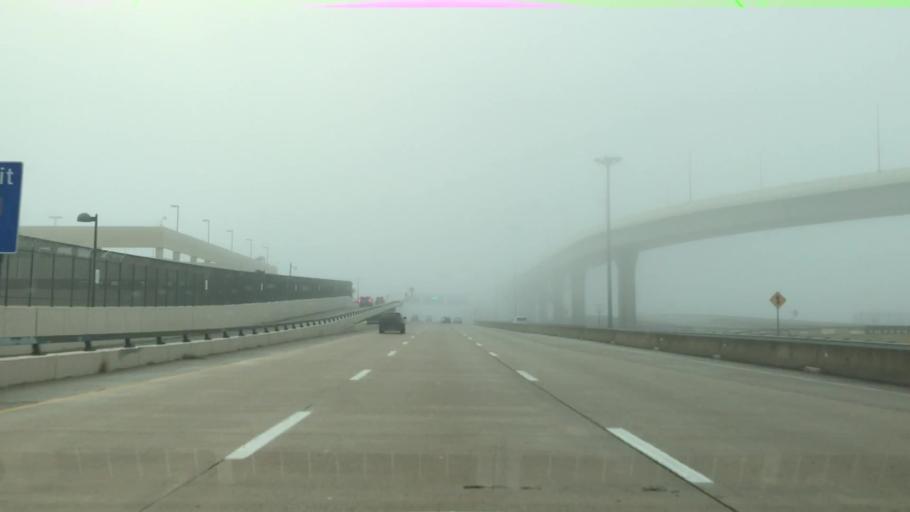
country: US
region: Texas
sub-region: Tarrant County
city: Grapevine
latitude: 32.8961
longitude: -97.0410
